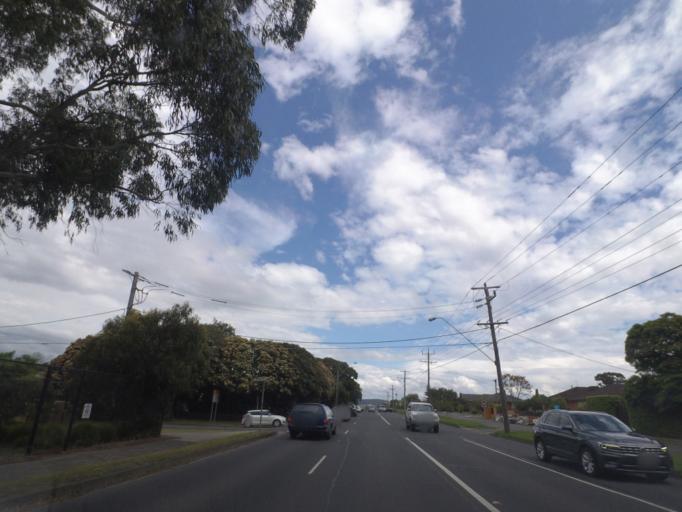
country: AU
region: Victoria
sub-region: Knox
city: Ferntree Gully
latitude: -37.8804
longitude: 145.2847
